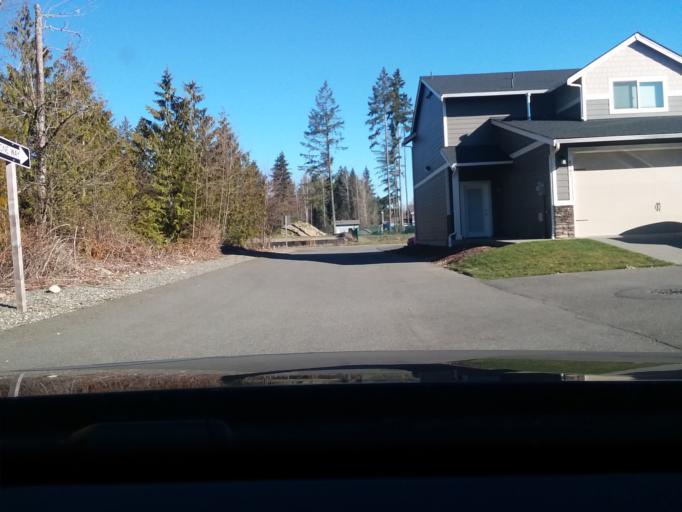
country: US
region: Washington
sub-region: Pierce County
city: Frederickson
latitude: 47.0979
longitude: -122.3191
